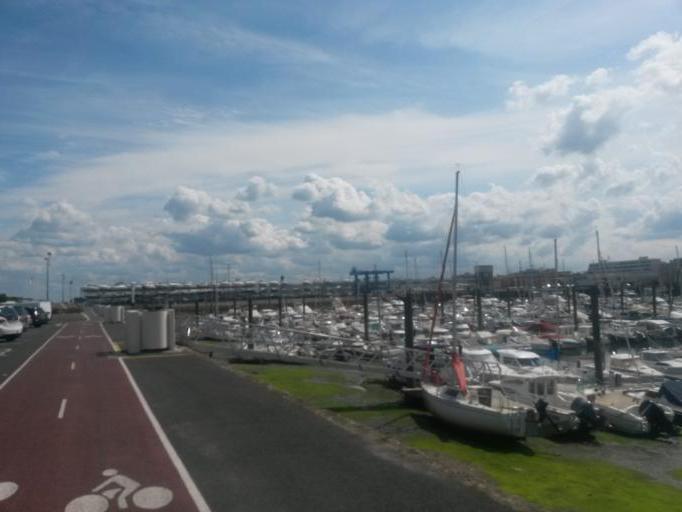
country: FR
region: Aquitaine
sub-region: Departement de la Gironde
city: Arcachon
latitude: 44.6606
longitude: -1.1459
